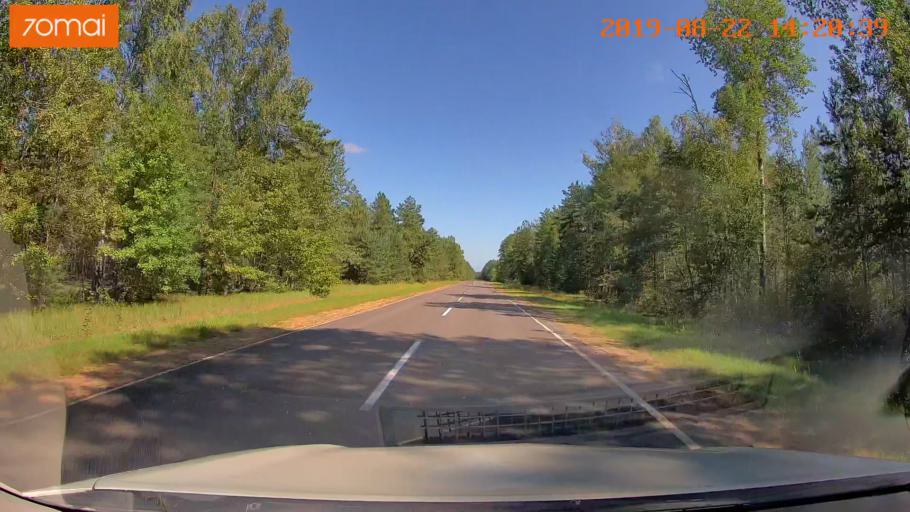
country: BY
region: Mogilev
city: Asipovichy
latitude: 53.2651
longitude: 28.5322
